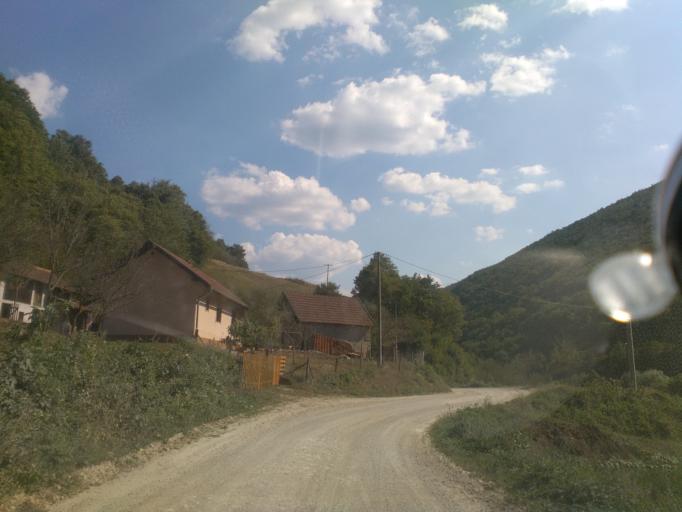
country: BA
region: Federation of Bosnia and Herzegovina
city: Orasac
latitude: 44.5104
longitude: 16.1276
